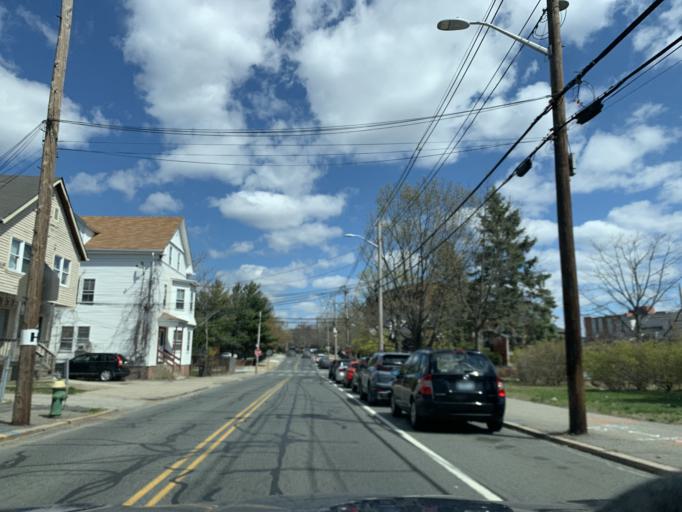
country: US
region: Rhode Island
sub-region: Providence County
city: Providence
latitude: 41.8112
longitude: -71.4154
